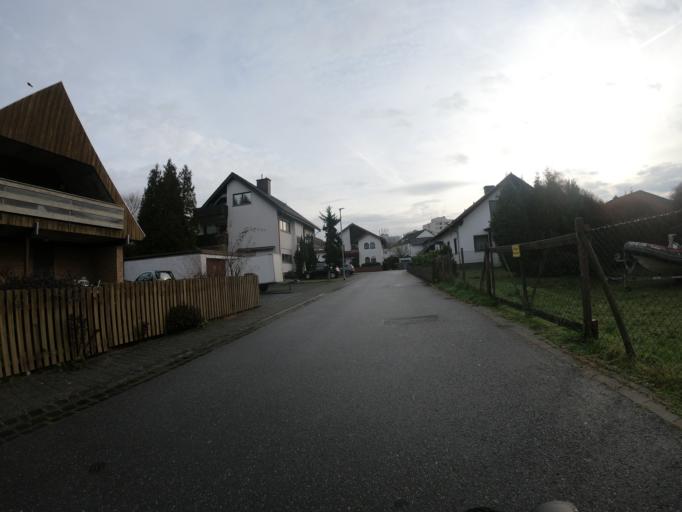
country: DE
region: Hesse
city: Morfelden-Walldorf
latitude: 49.9803
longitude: 8.5556
